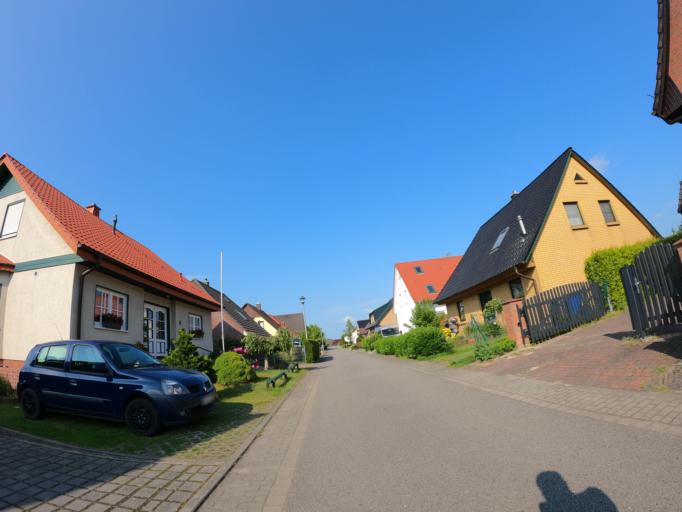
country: DE
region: Mecklenburg-Vorpommern
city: Stralsund
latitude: 54.2932
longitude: 13.0644
